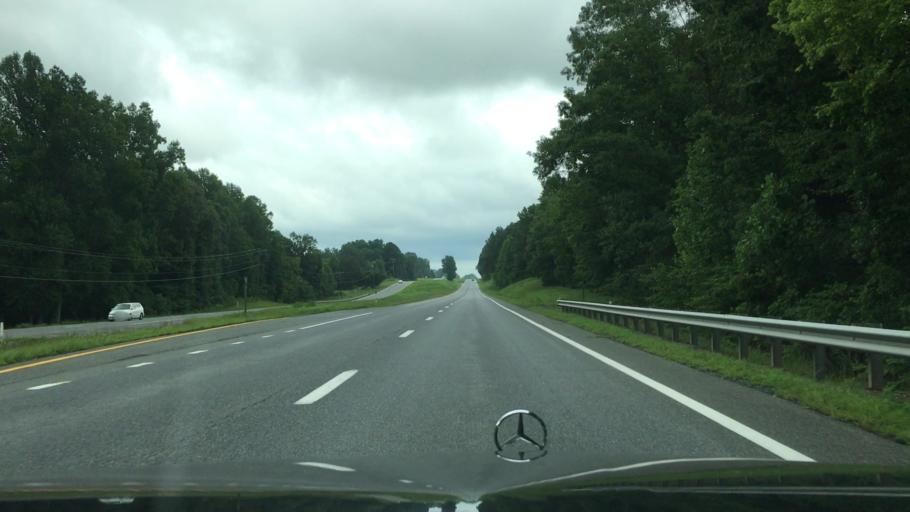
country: US
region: Virginia
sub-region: Appomattox County
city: Appomattox
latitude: 37.2825
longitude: -78.7095
